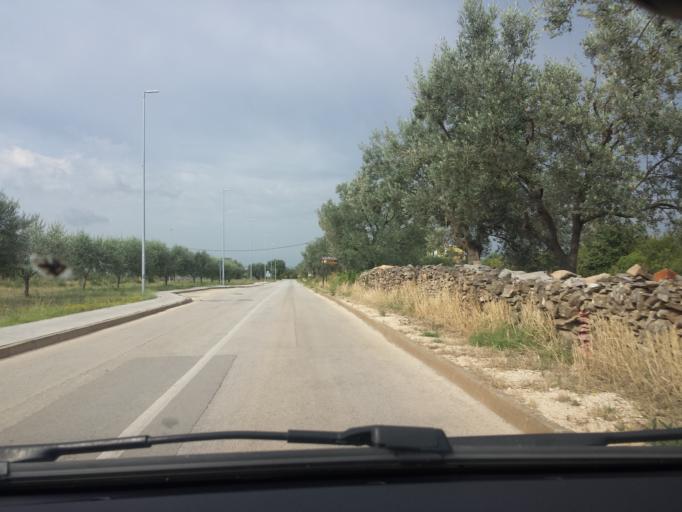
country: HR
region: Istarska
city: Galizana
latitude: 44.9248
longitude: 13.8649
